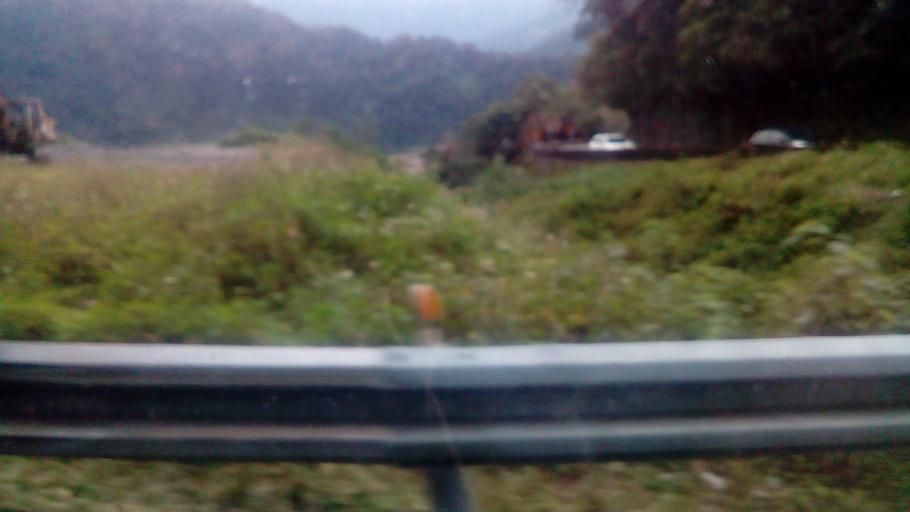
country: TW
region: Taiwan
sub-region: Yilan
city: Yilan
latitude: 24.5840
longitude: 121.4986
